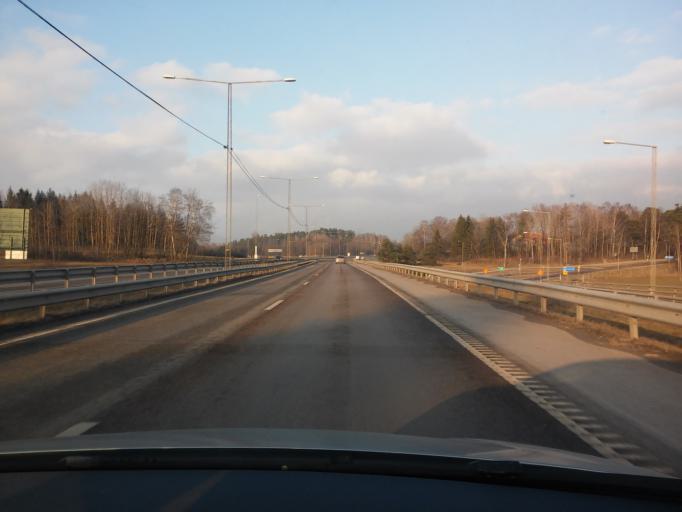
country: SE
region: Stockholm
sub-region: Taby Kommun
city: Taby
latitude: 59.4643
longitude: 18.1485
